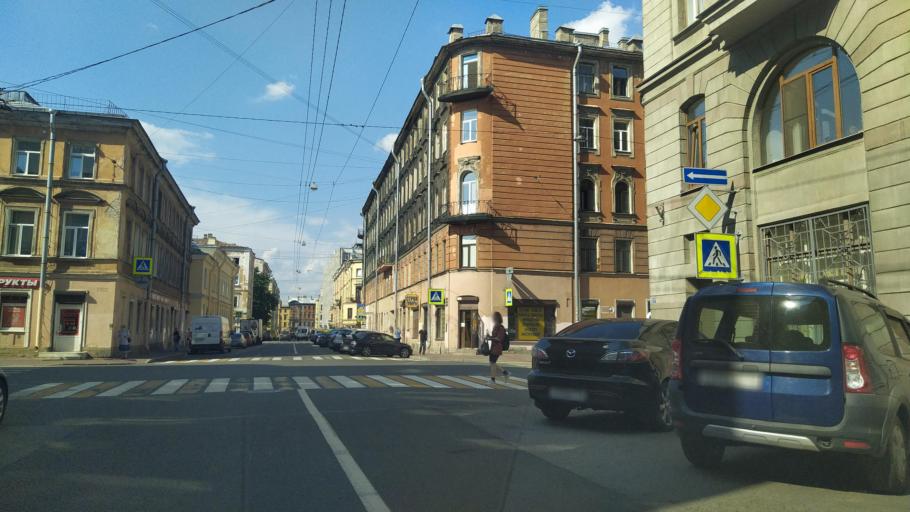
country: RU
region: St.-Petersburg
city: Saint Petersburg
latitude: 59.9129
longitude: 30.3140
